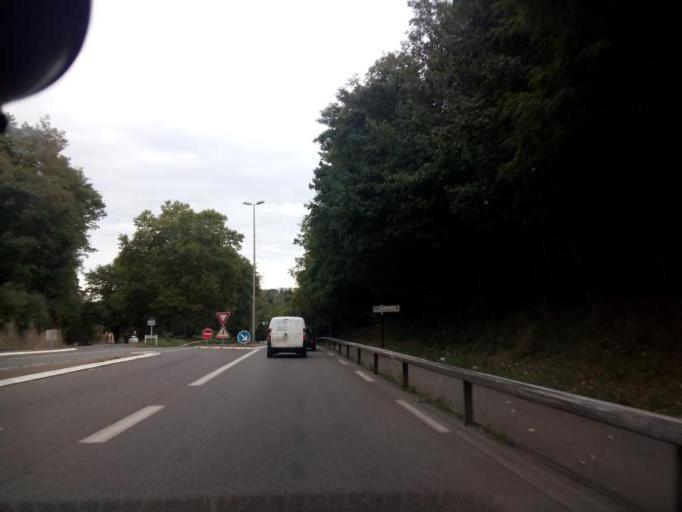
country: FR
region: Rhone-Alpes
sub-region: Departement du Rhone
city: Ecully
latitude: 45.7662
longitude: 4.7704
